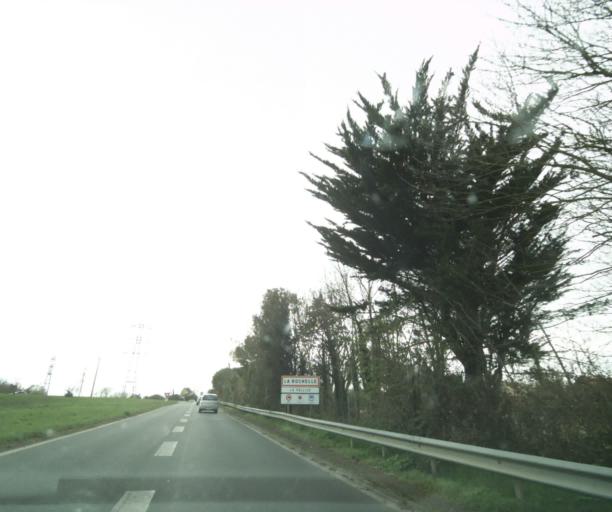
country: FR
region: Poitou-Charentes
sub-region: Departement de la Charente-Maritime
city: La Rochelle
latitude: 46.1661
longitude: -1.1931
